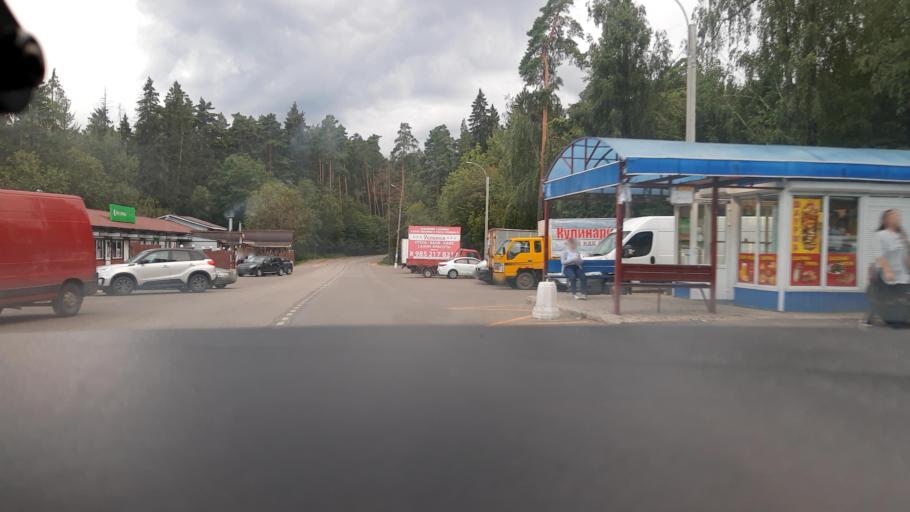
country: RU
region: Moskovskaya
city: Lesnoy Gorodok
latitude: 55.6787
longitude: 37.1884
